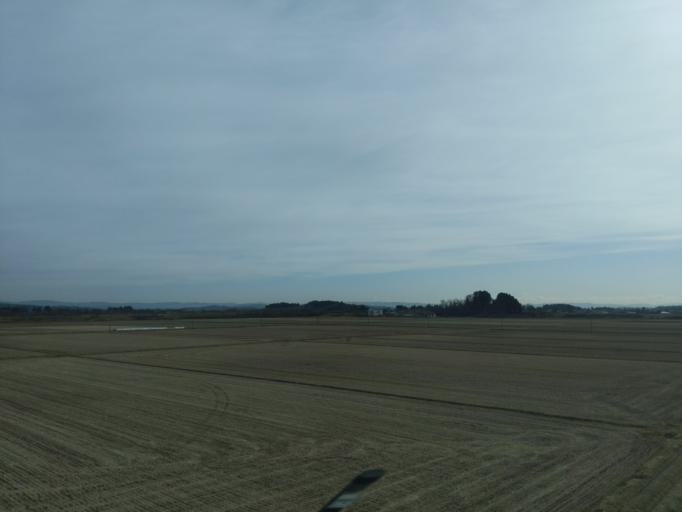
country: JP
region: Iwate
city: Ichinoseki
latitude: 38.7818
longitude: 141.0904
